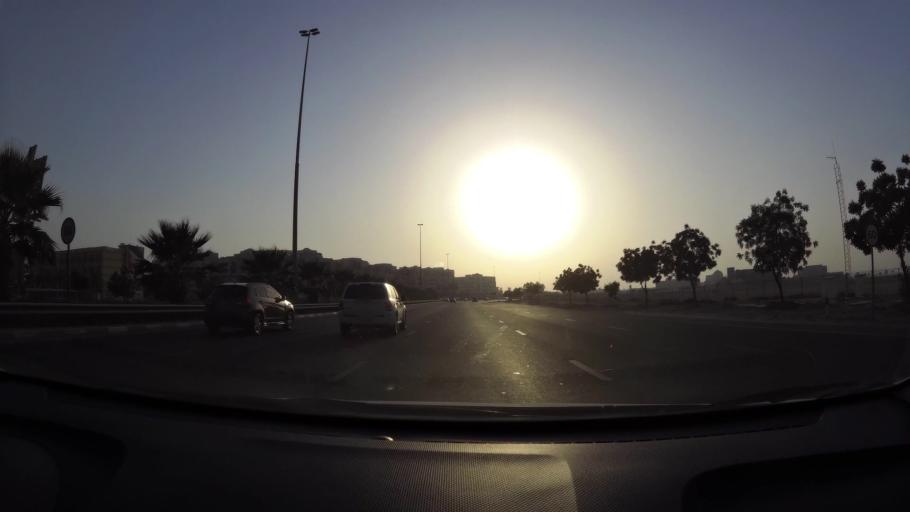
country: AE
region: Ash Shariqah
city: Sharjah
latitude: 25.2908
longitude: 55.3566
